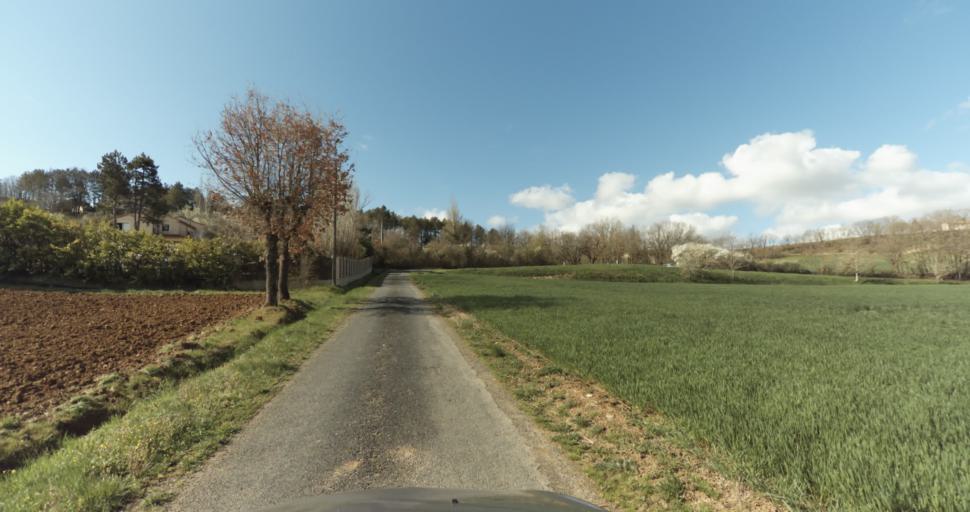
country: FR
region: Midi-Pyrenees
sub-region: Departement du Tarn
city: Puygouzon
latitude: 43.8699
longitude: 2.1741
